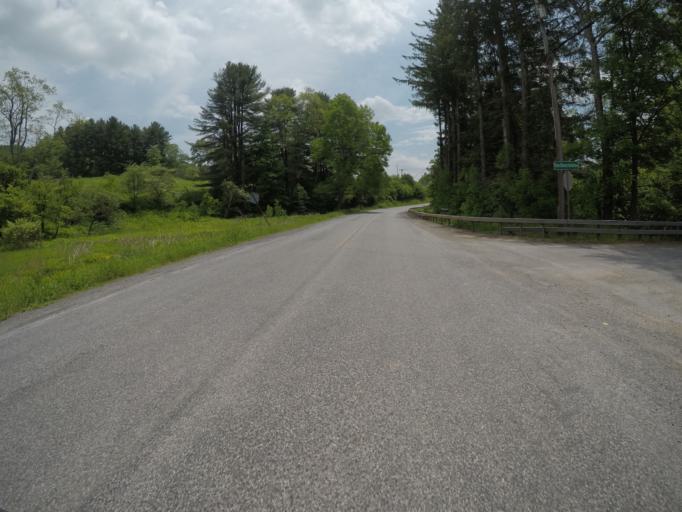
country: US
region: New York
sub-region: Delaware County
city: Stamford
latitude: 42.2041
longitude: -74.6776
